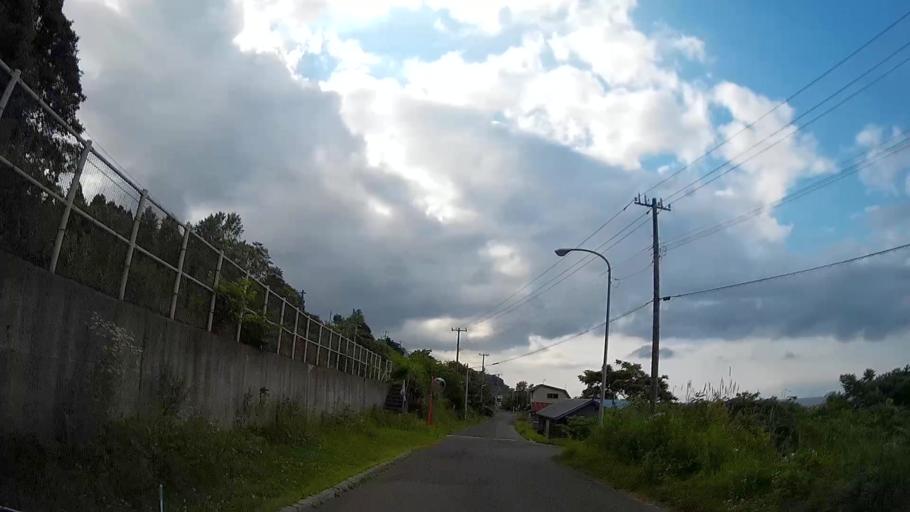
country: JP
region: Hokkaido
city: Nanae
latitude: 42.1141
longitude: 140.5457
